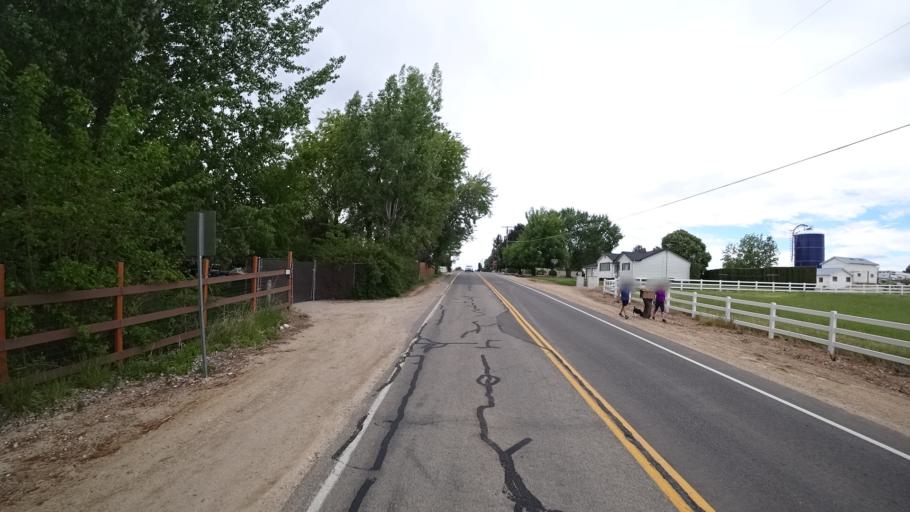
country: US
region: Idaho
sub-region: Ada County
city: Meridian
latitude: 43.5765
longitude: -116.4137
